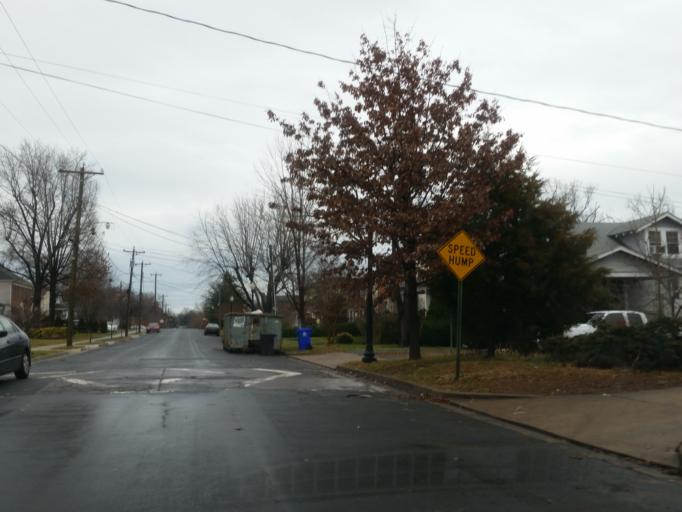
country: US
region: Virginia
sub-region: Arlington County
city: Arlington
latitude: 38.8629
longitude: -77.0989
